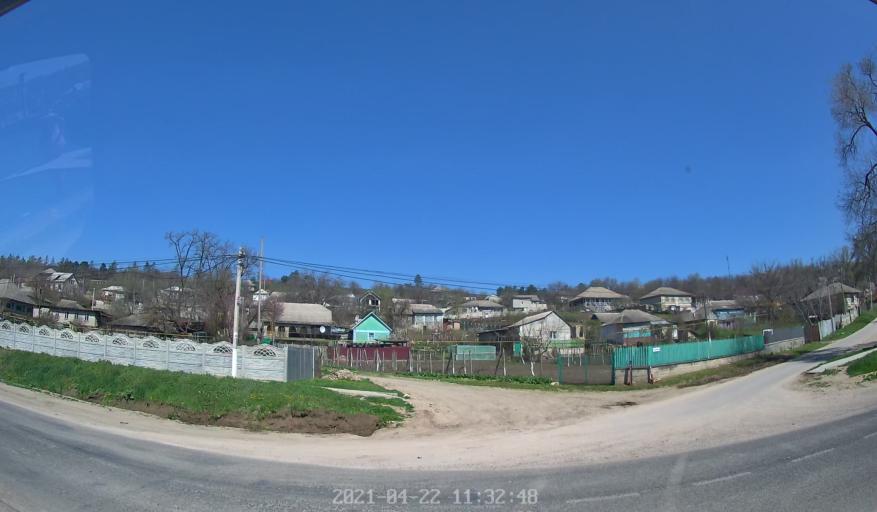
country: MD
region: Chisinau
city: Ciorescu
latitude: 47.1357
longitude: 28.9545
